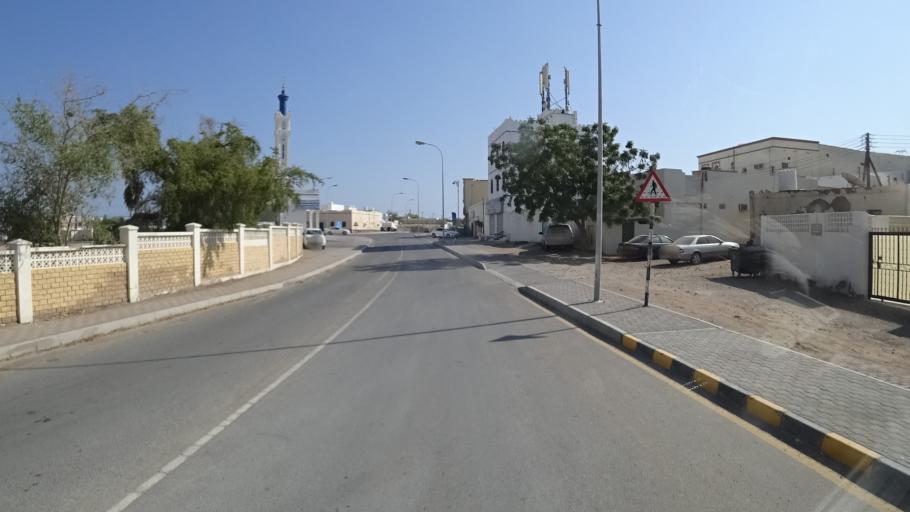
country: OM
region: Ash Sharqiyah
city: Sur
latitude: 22.5720
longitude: 59.5269
